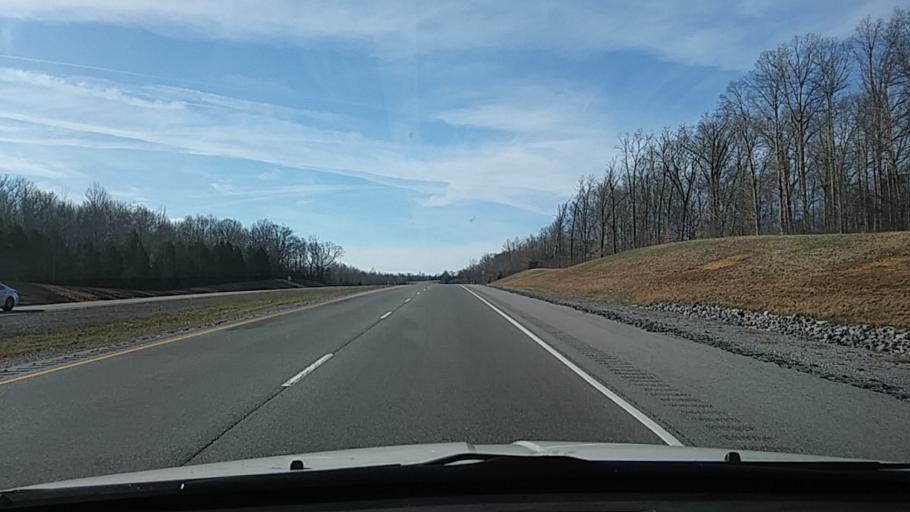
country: US
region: Tennessee
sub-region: Sumner County
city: Portland
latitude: 36.5341
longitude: -86.5092
